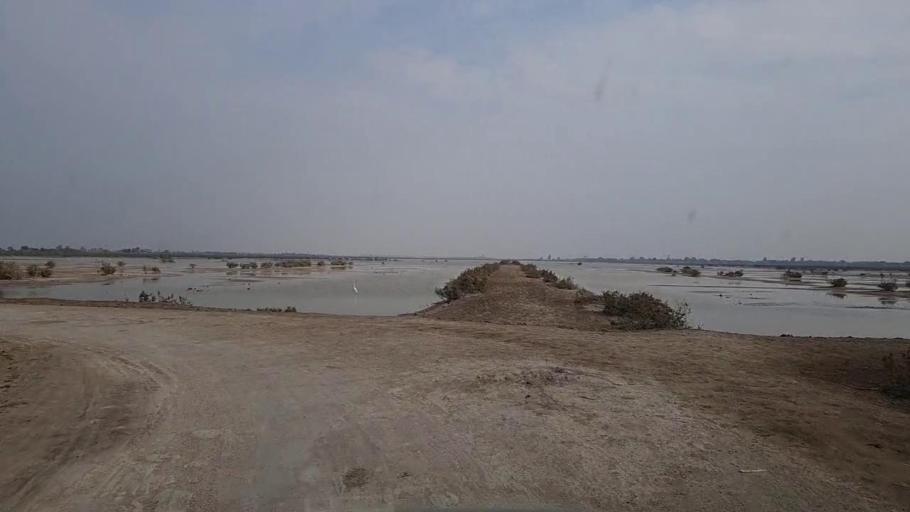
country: PK
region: Sindh
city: Mirwah Gorchani
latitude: 25.3573
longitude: 69.0395
